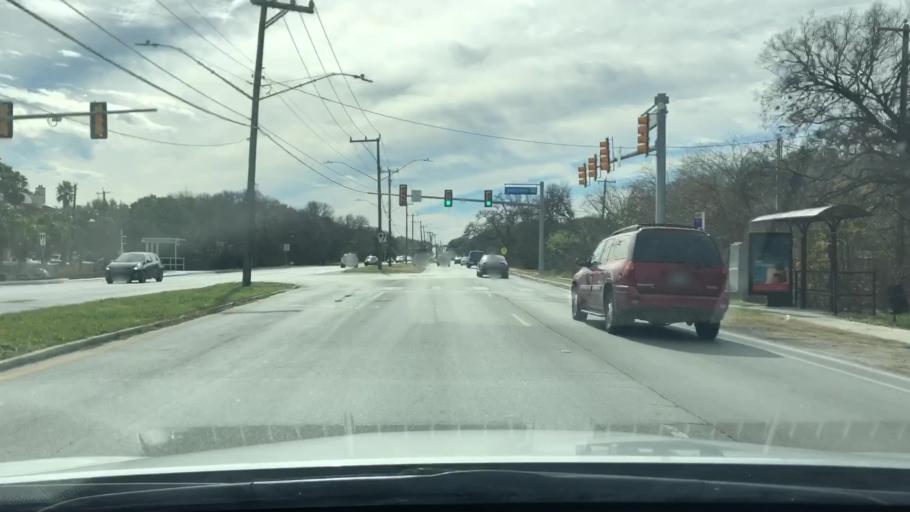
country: US
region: Texas
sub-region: Bexar County
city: Terrell Hills
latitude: 29.5096
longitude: -98.4346
